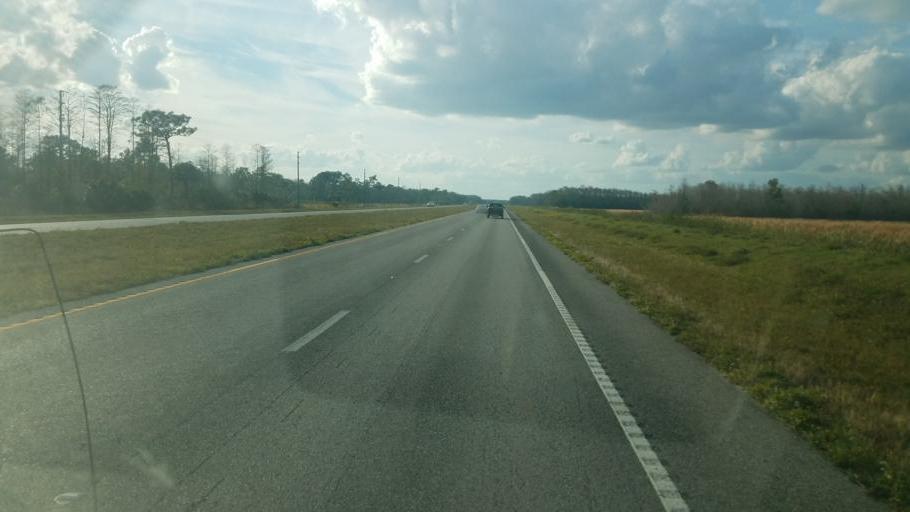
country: US
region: Florida
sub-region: Osceola County
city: Saint Cloud
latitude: 28.1399
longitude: -81.0471
